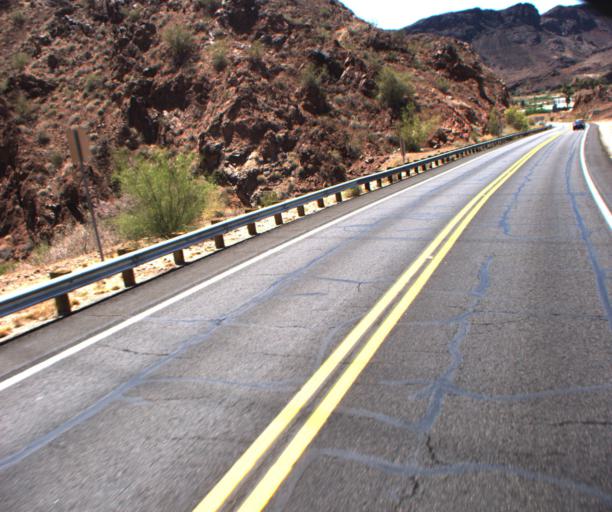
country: US
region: Arizona
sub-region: La Paz County
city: Cienega Springs
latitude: 34.2882
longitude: -114.1319
